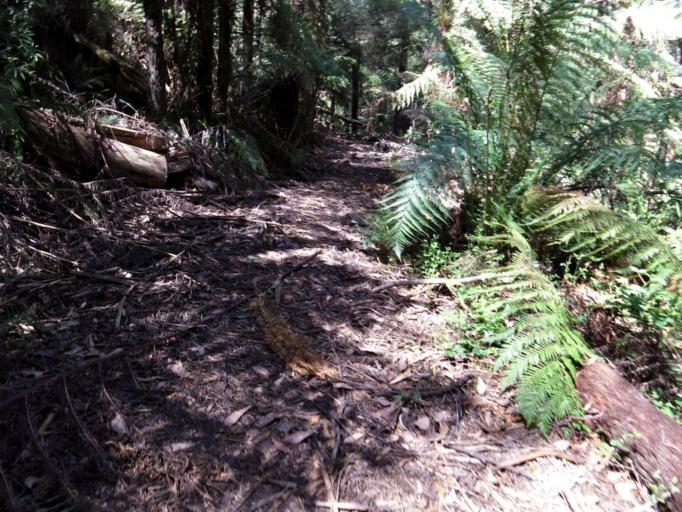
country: AU
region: Victoria
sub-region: Yarra Ranges
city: Millgrove
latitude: -37.8513
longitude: 145.7600
